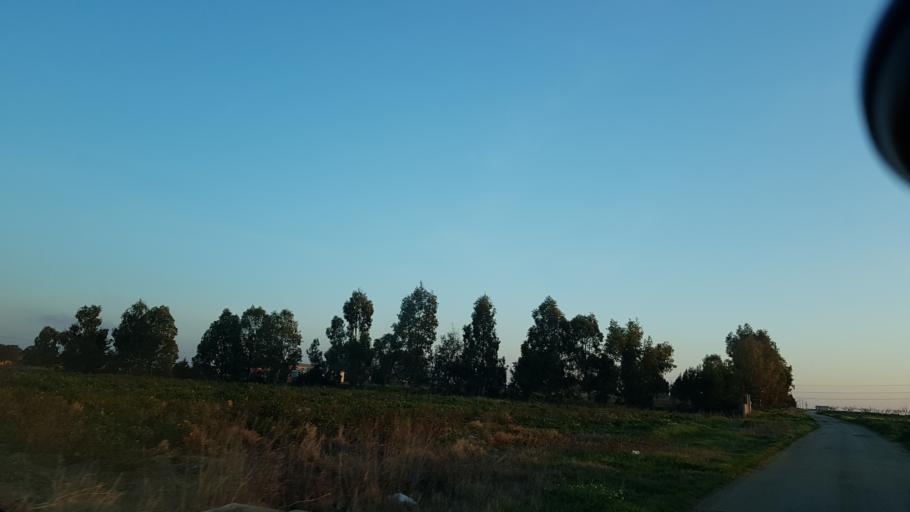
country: IT
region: Apulia
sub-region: Provincia di Brindisi
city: La Rosa
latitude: 40.6022
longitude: 17.9517
